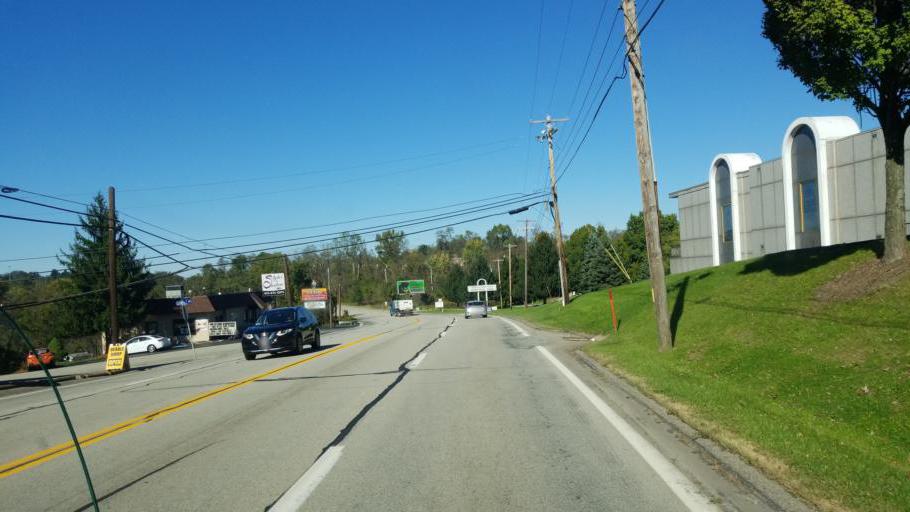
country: US
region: Pennsylvania
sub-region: Westmoreland County
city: Trafford
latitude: 40.3586
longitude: -79.7704
